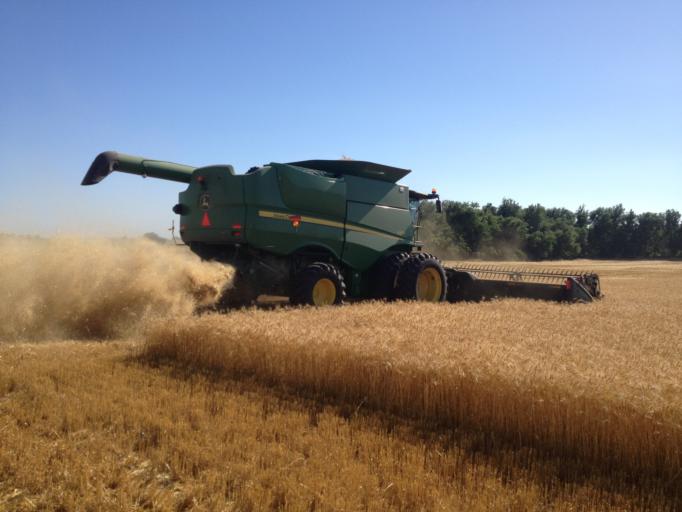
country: US
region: Kansas
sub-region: Rice County
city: Lyons
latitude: 38.3178
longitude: -98.3592
